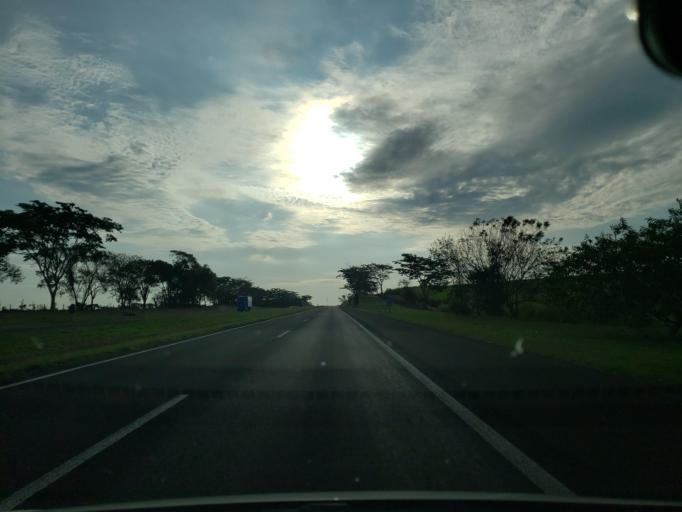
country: BR
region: Sao Paulo
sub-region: Mirandopolis
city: Mirandopolis
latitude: -21.1130
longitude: -51.0203
